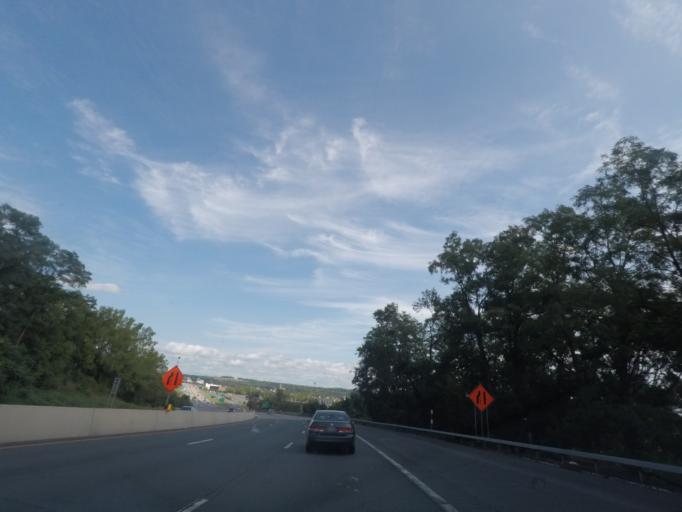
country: US
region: New York
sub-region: Albany County
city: Albany
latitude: 42.6327
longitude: -73.7656
